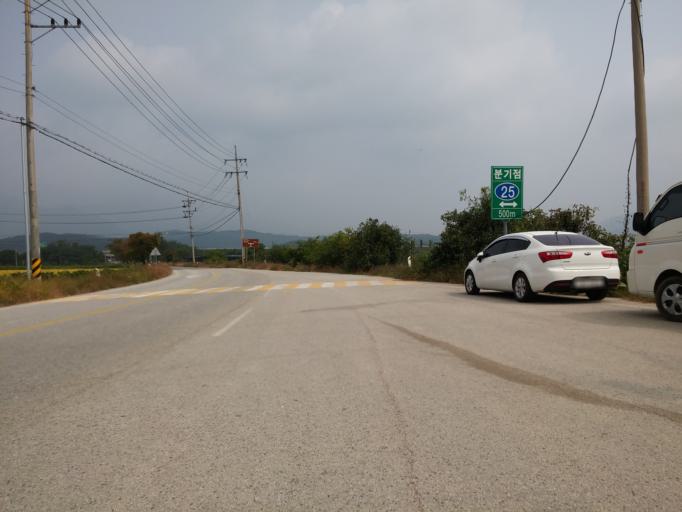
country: KR
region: Chungcheongbuk-do
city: Yong-dong
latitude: 36.4344
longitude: 127.8070
